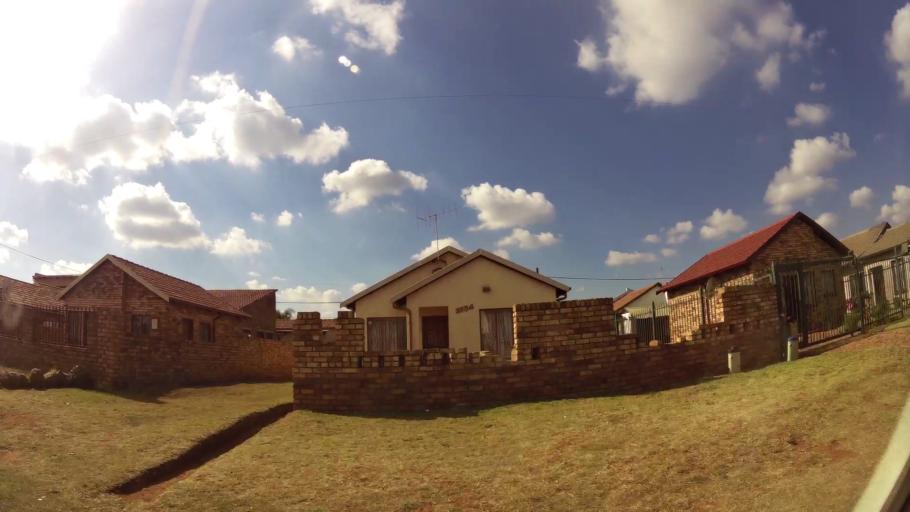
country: ZA
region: Gauteng
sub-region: City of Tshwane Metropolitan Municipality
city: Cullinan
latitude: -25.7015
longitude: 28.4169
